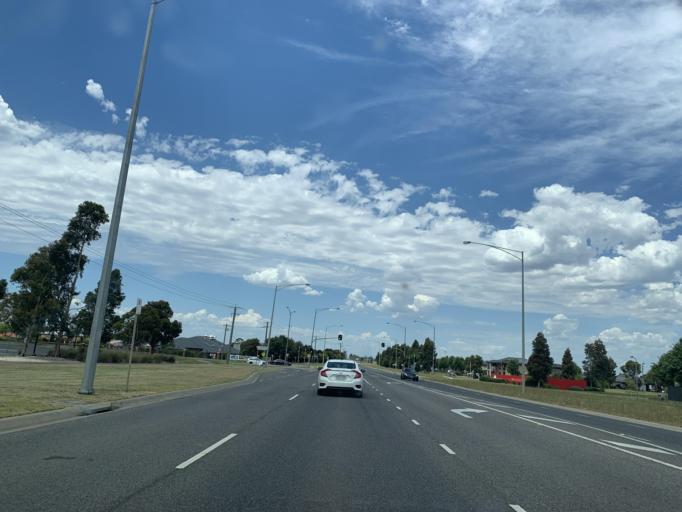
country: AU
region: Victoria
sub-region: Casey
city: Cranbourne East
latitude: -38.1149
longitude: 145.2975
